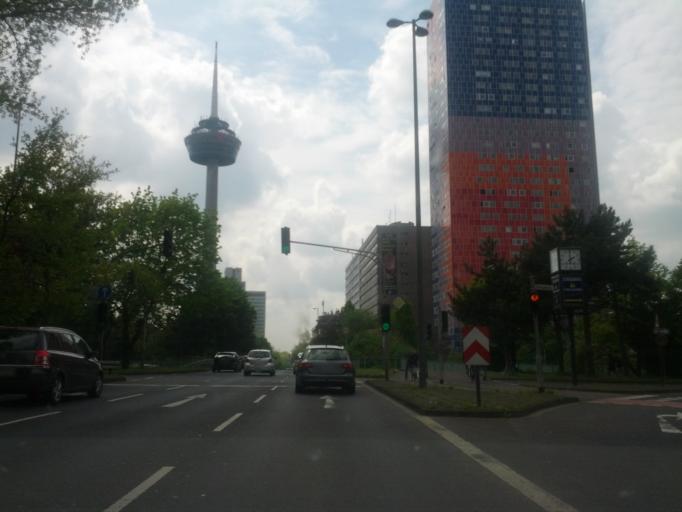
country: DE
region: North Rhine-Westphalia
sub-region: Regierungsbezirk Koln
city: Neuehrenfeld
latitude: 50.9511
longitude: 6.9355
